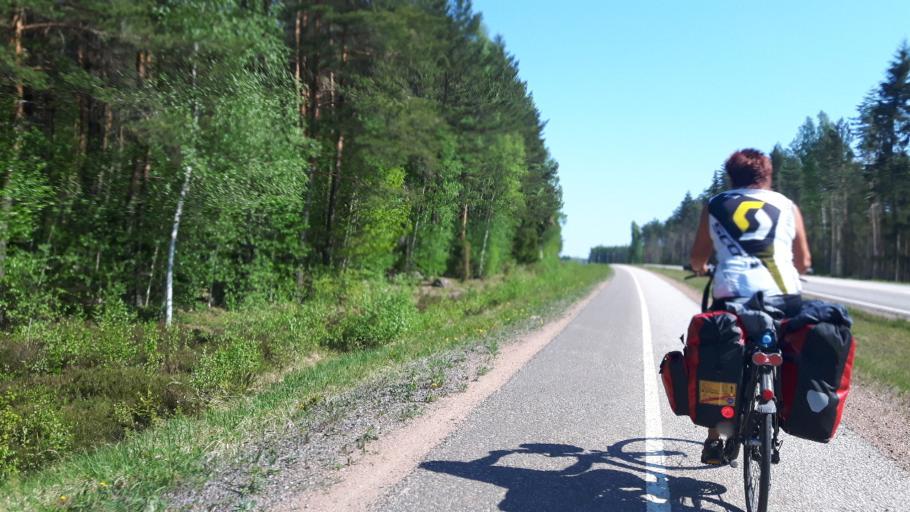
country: FI
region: Kymenlaakso
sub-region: Kotka-Hamina
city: Pyhtaeae
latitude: 60.4890
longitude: 26.5047
